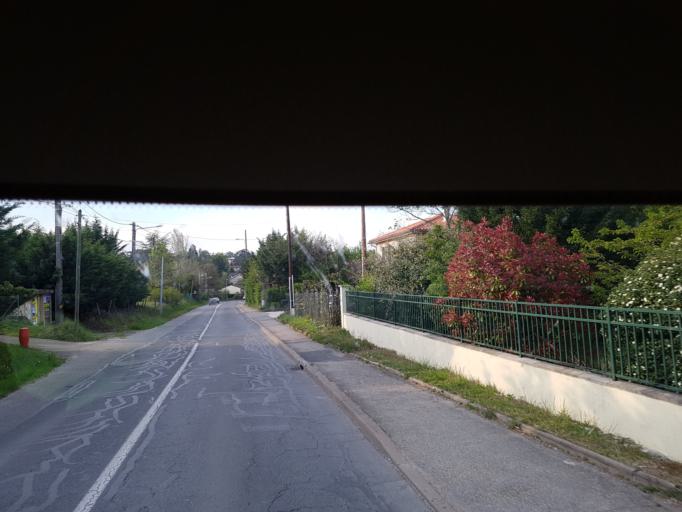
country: FR
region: Rhone-Alpes
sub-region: Departement du Rhone
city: Grezieu-la-Varenne
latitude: 45.7420
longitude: 4.6906
